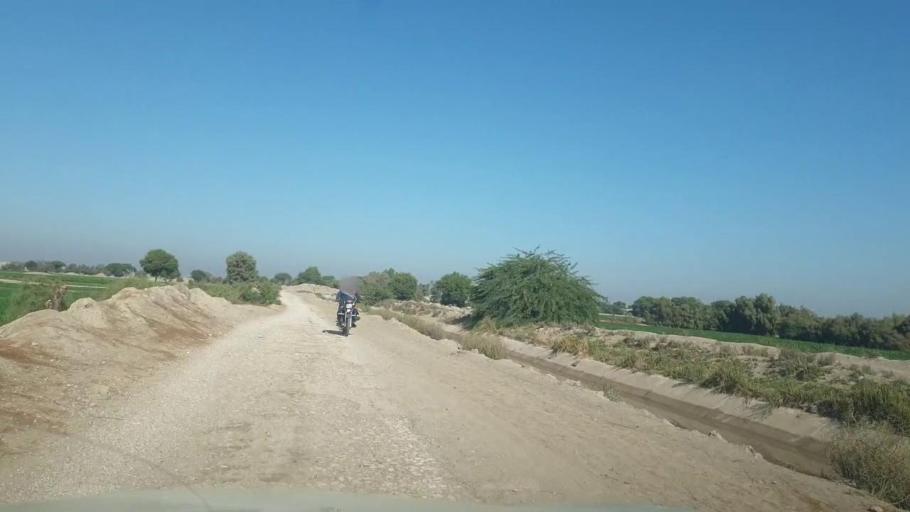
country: PK
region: Sindh
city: Bhan
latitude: 26.5579
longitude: 67.6303
